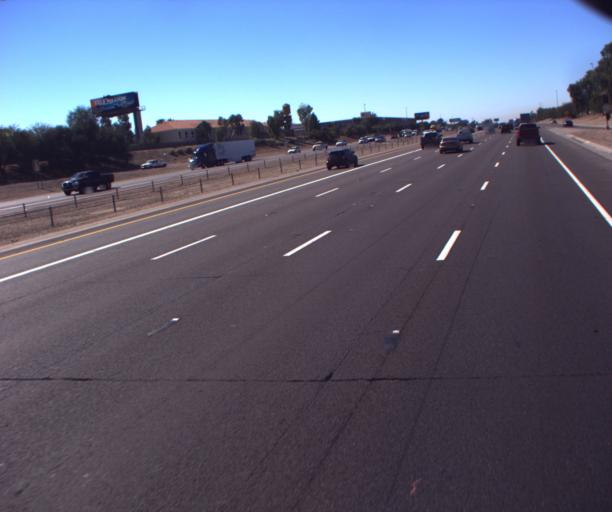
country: US
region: Arizona
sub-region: Maricopa County
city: Glendale
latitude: 33.4631
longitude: -112.1711
